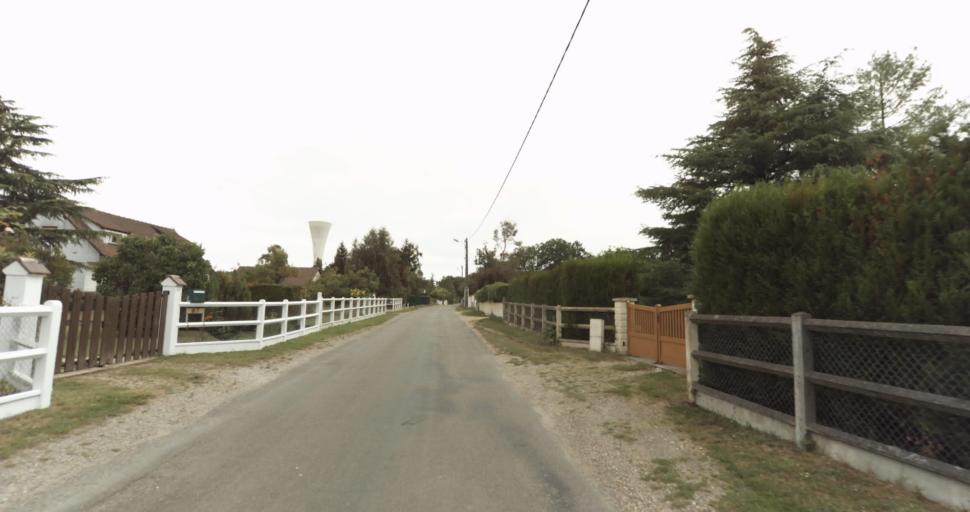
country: FR
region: Haute-Normandie
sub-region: Departement de l'Eure
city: Saint-Germain-sur-Avre
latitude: 48.7705
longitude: 1.2631
